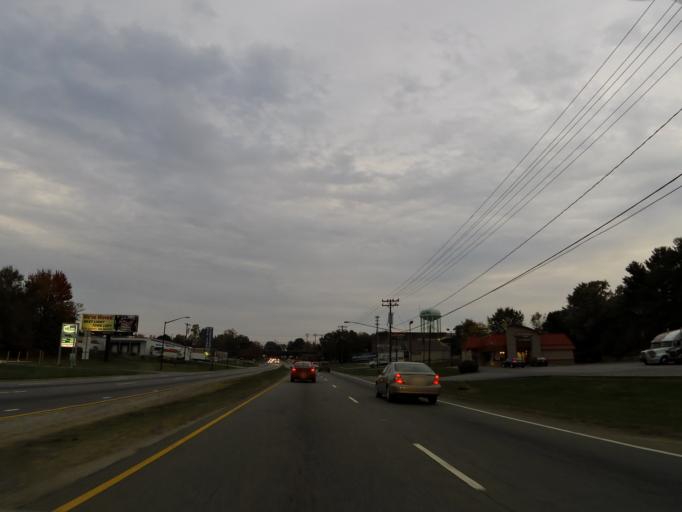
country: US
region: North Carolina
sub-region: Catawba County
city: Longview
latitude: 35.7342
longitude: -81.3655
